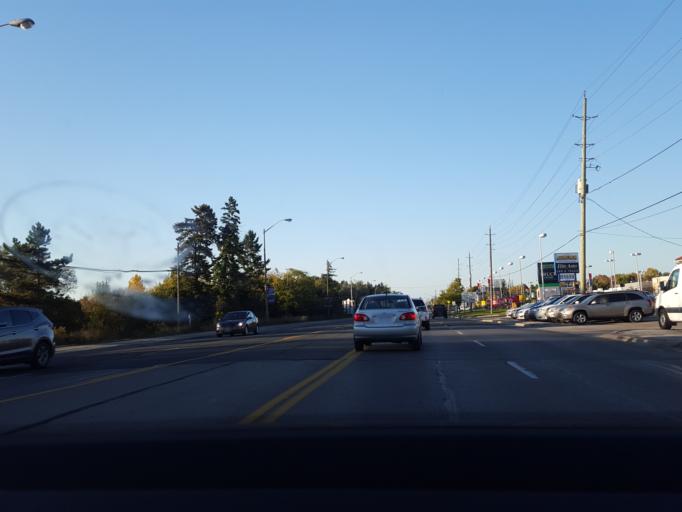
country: CA
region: Ontario
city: Newmarket
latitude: 44.0105
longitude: -79.4701
